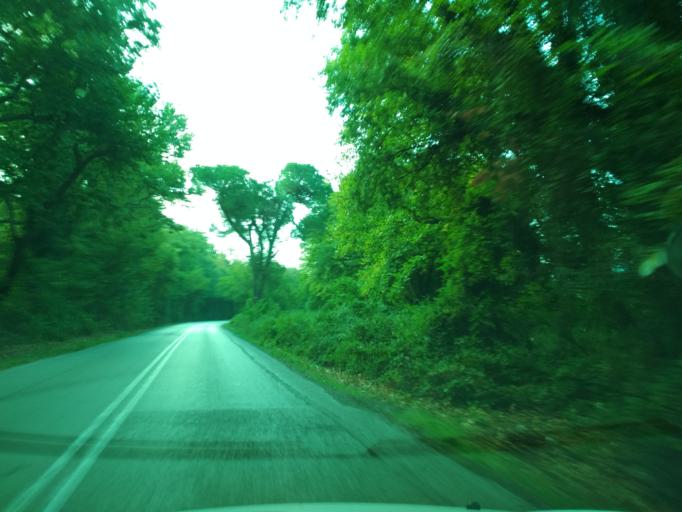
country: GR
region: Central Greece
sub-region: Nomos Evvoias
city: Prokopion
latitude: 38.7604
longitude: 23.4798
